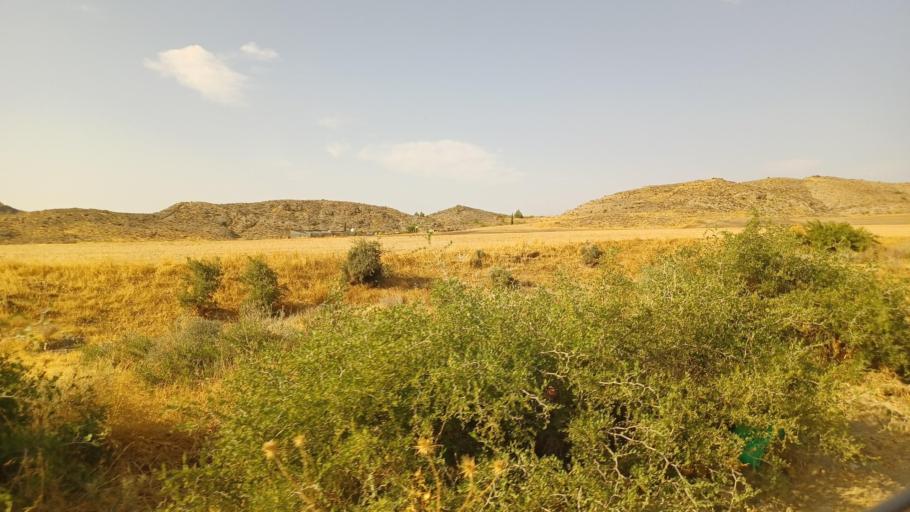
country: CY
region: Larnaka
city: Athienou
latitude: 35.0133
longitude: 33.5631
